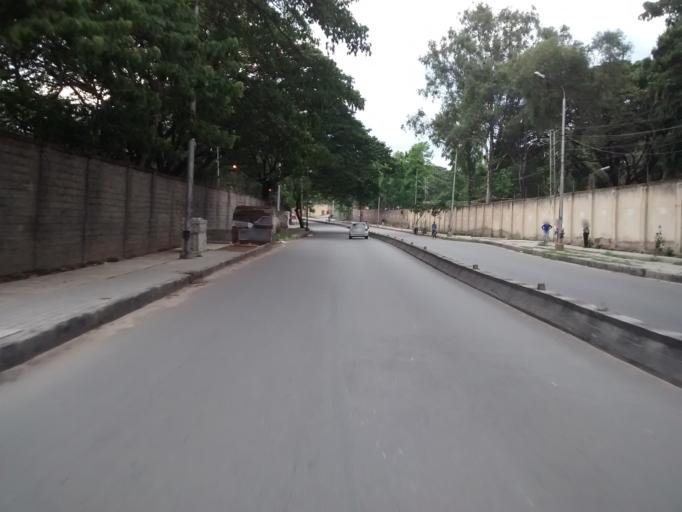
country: IN
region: Karnataka
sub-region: Bangalore Urban
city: Bangalore
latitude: 12.9572
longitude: 77.6740
